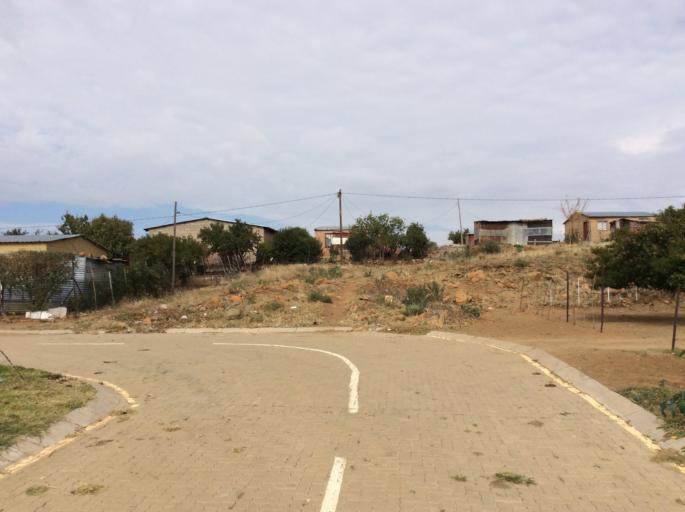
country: LS
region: Mafeteng
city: Mafeteng
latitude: -29.7205
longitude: 27.0072
